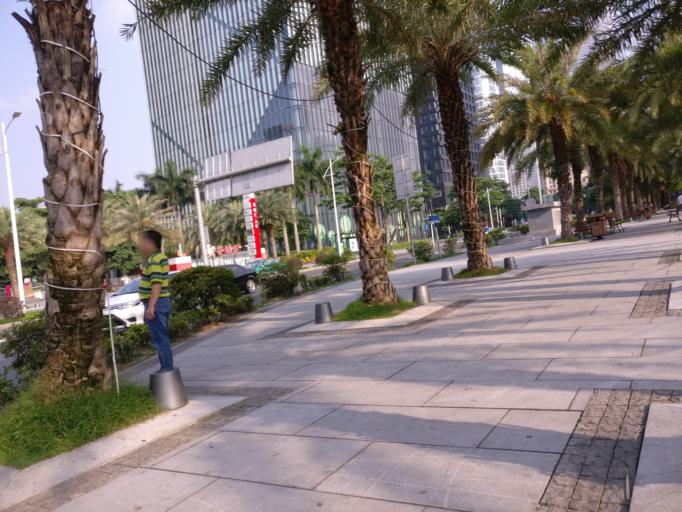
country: CN
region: Guangdong
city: Wushan
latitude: 23.1295
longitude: 113.3197
